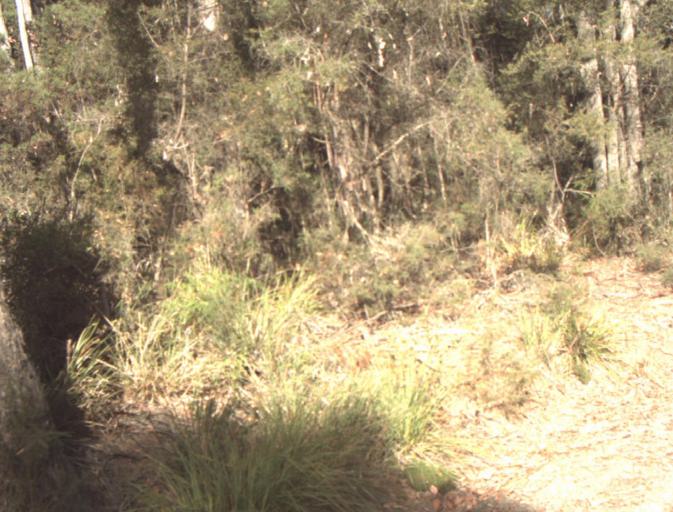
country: AU
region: Tasmania
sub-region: Launceston
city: Mayfield
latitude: -41.2640
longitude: 147.2313
